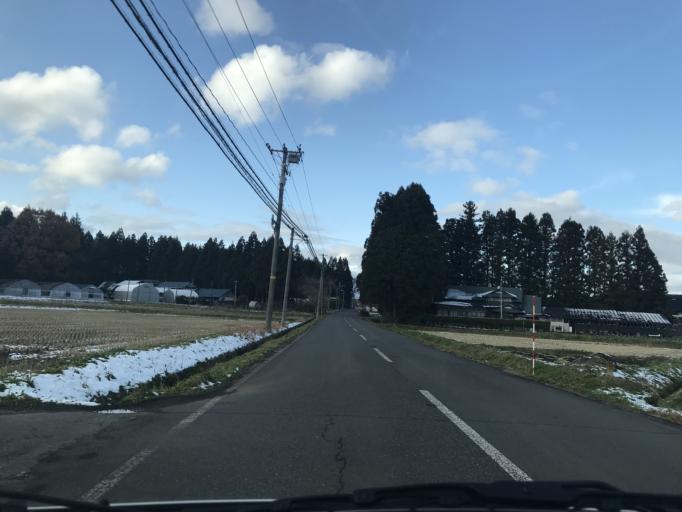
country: JP
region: Iwate
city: Kitakami
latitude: 39.2191
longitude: 141.0460
